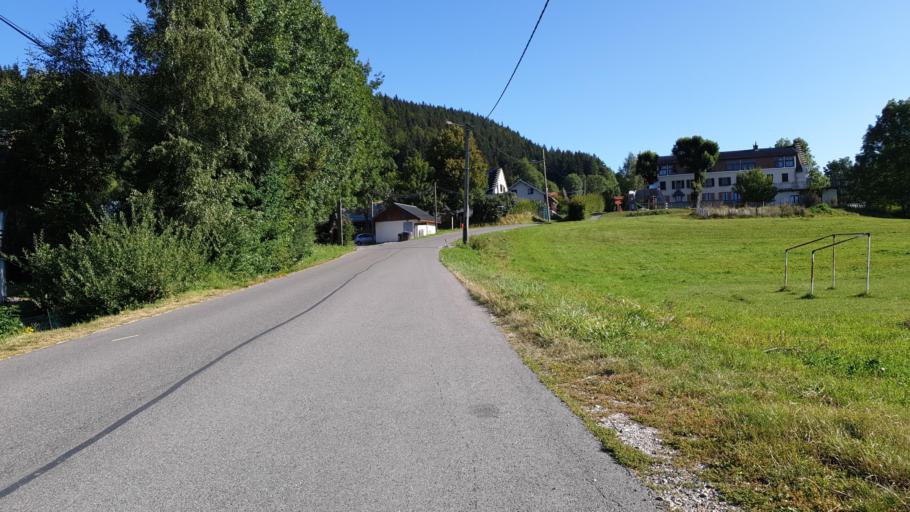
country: FR
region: Rhone-Alpes
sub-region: Departement de l'Isere
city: Autrans
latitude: 45.1843
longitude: 5.5455
